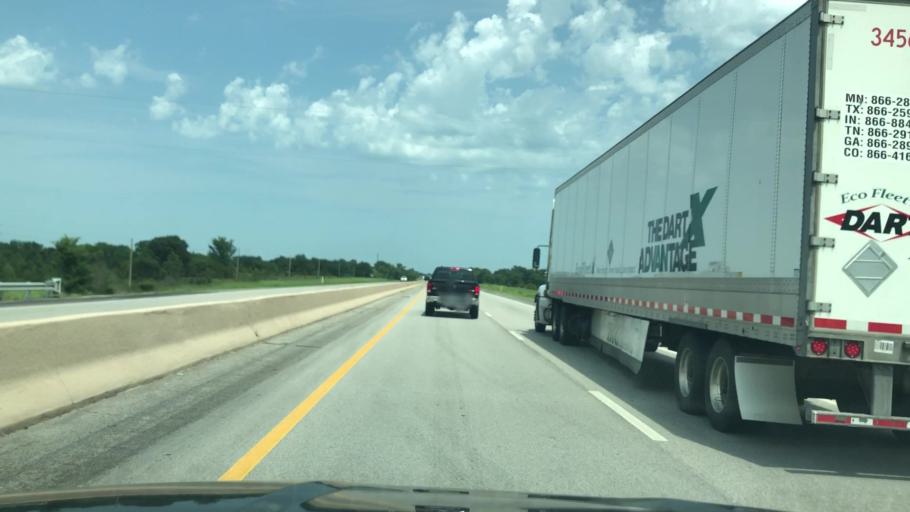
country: US
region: Oklahoma
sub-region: Rogers County
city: Verdigris
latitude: 36.2208
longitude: -95.6864
